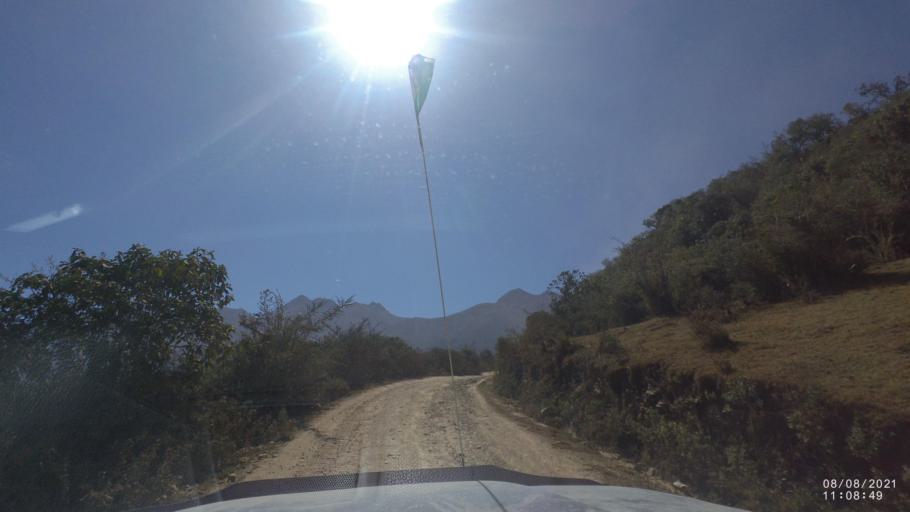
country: BO
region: Cochabamba
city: Colchani
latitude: -16.7610
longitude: -66.6788
